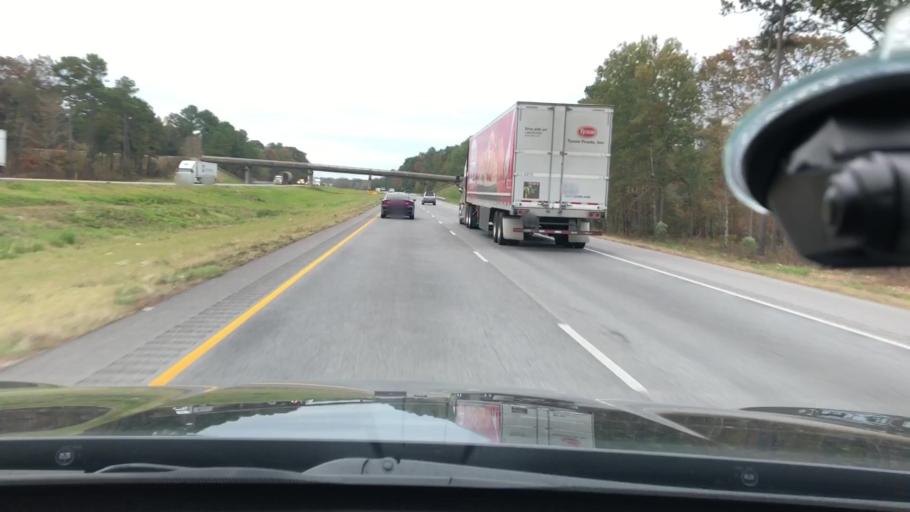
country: US
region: Arkansas
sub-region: Hempstead County
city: Hope
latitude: 33.6292
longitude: -93.7307
